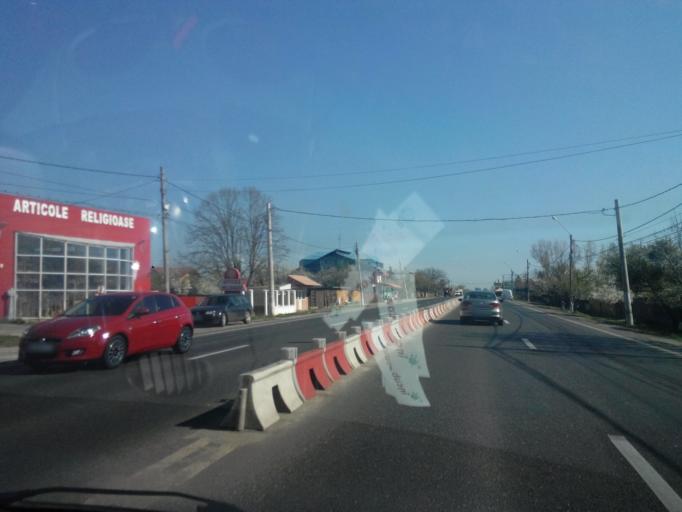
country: RO
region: Ilfov
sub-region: Comuna Ciolpani
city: Ciolpani
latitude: 44.7156
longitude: 26.1004
